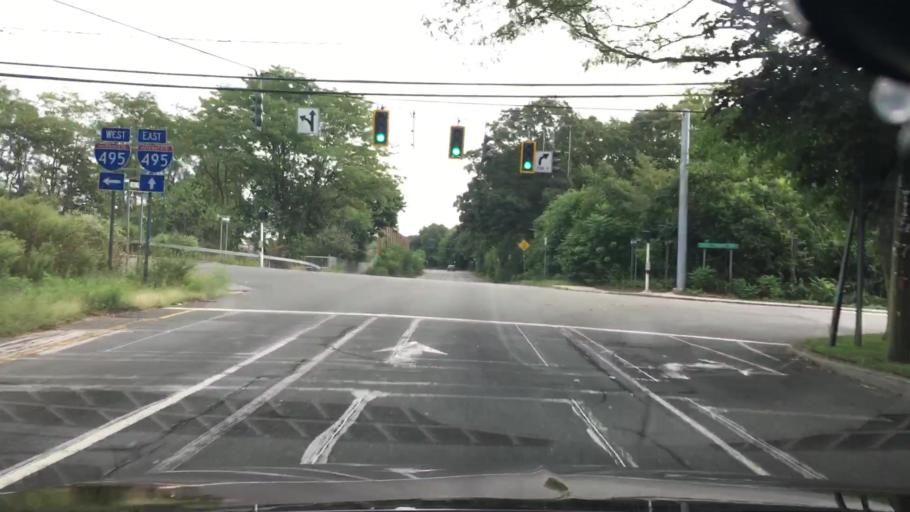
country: US
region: New York
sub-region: Suffolk County
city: Dix Hills
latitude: 40.8020
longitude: -73.3205
